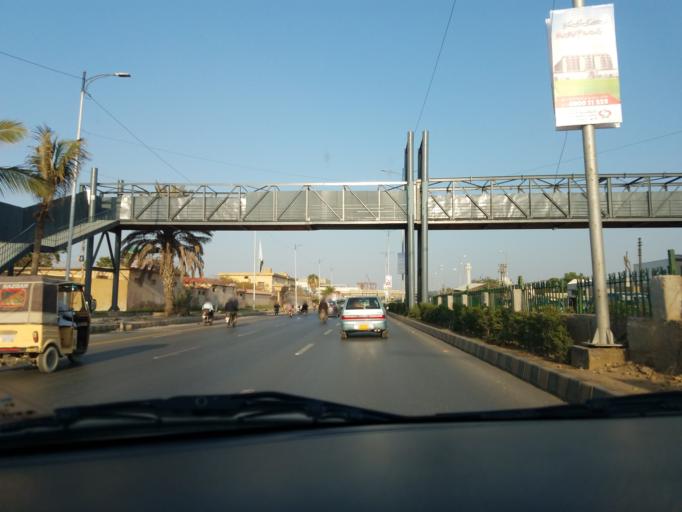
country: PK
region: Sindh
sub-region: Karachi District
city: Karachi
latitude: 24.8831
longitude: 67.1139
